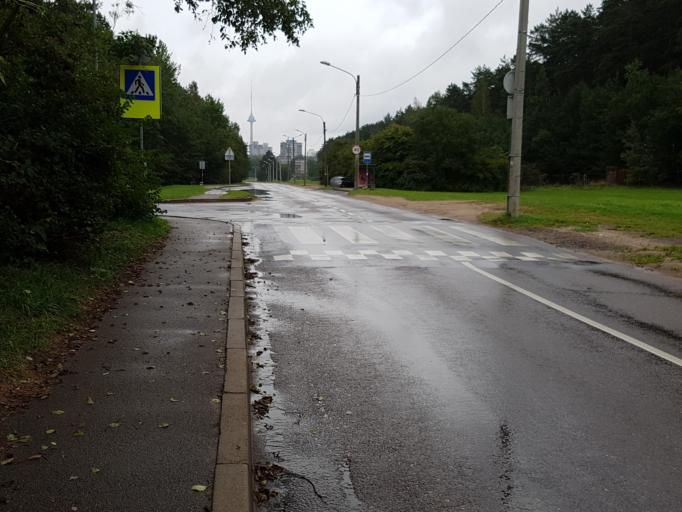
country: LT
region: Vilnius County
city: Lazdynai
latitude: 54.6660
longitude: 25.1951
